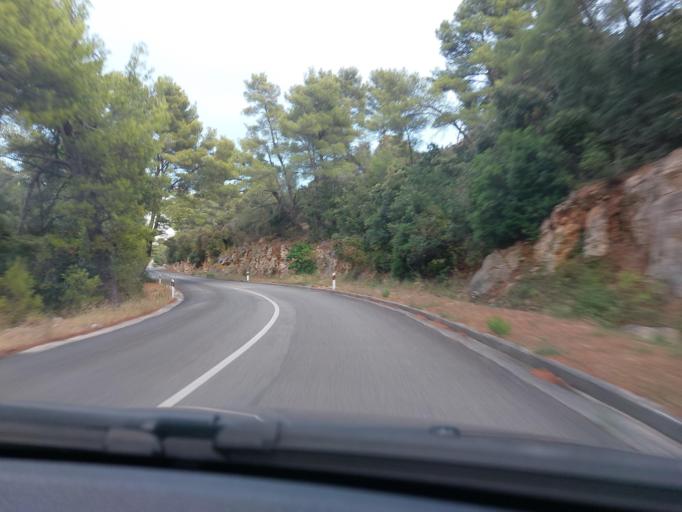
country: HR
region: Dubrovacko-Neretvanska
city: Smokvica
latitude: 42.7662
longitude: 16.8869
